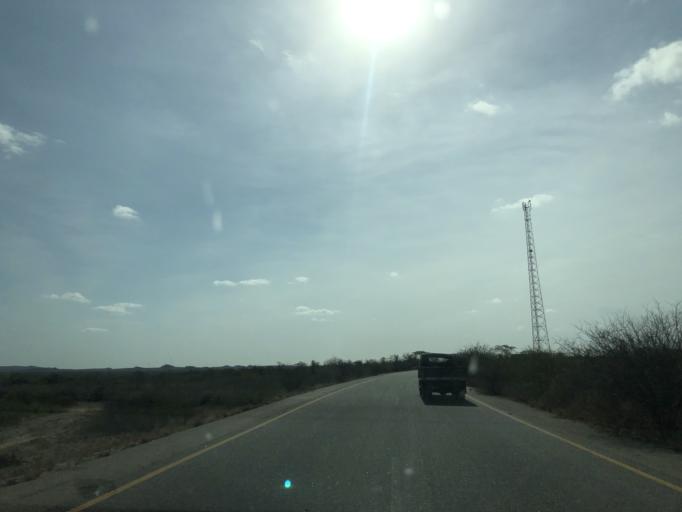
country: AO
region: Benguela
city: Benguela
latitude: -12.8937
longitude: 13.4801
